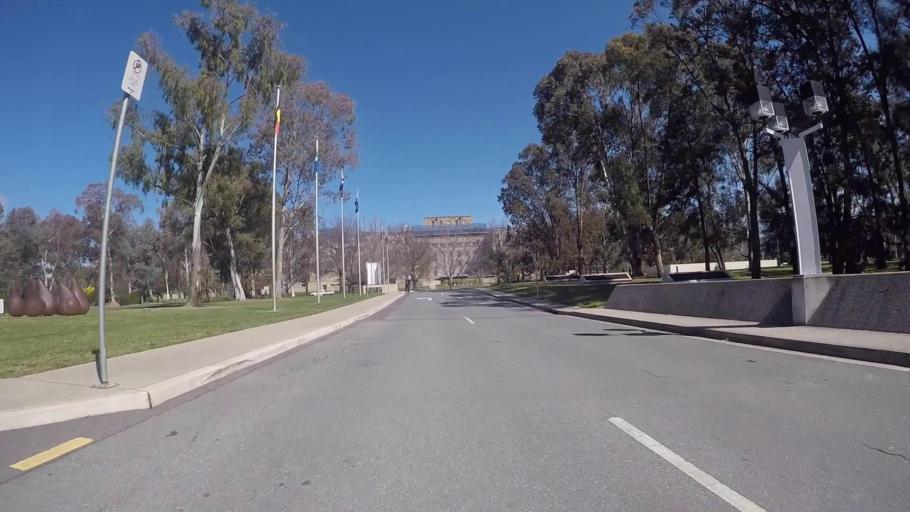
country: AU
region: Australian Capital Territory
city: Forrest
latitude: -35.3007
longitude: 149.1357
